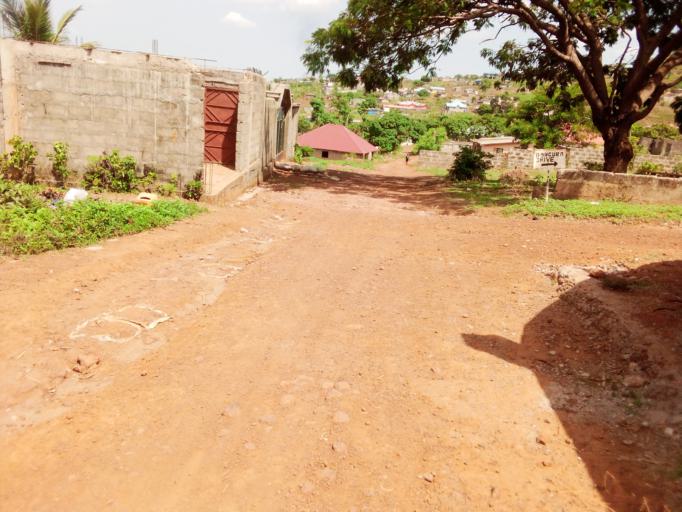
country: SL
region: Western Area
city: Waterloo
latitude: 8.3505
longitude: -13.0844
